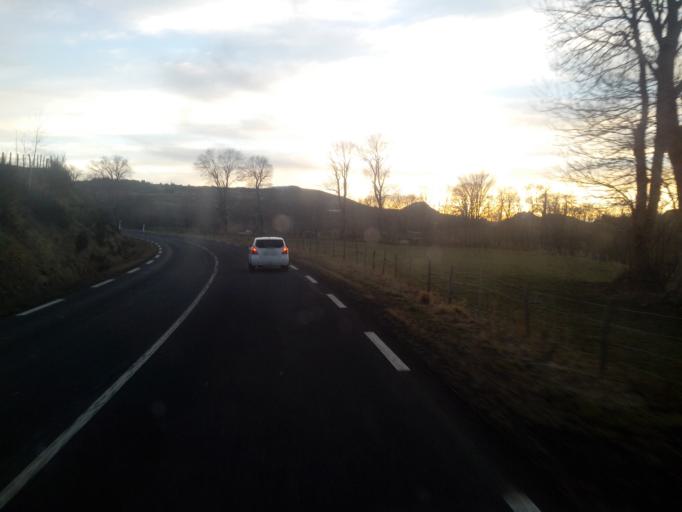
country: FR
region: Auvergne
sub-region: Departement du Cantal
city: Murat
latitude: 45.1521
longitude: 2.8127
